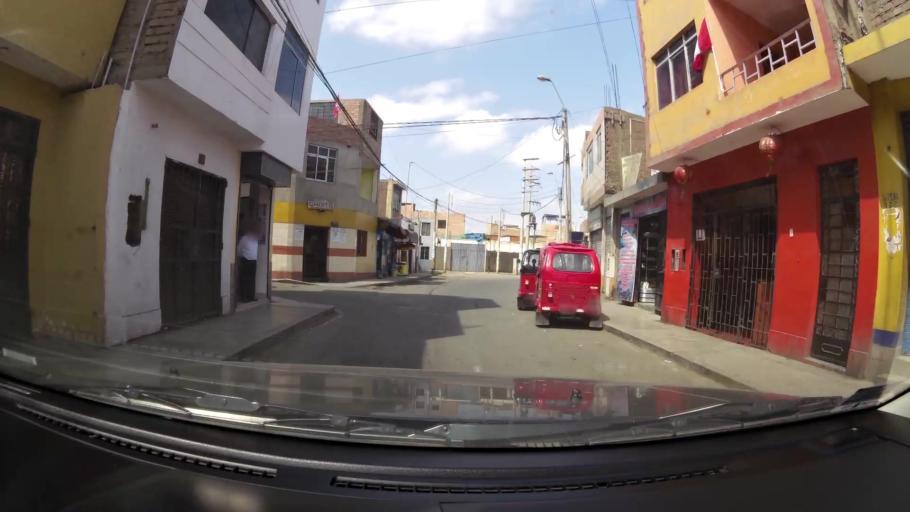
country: PE
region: Lima
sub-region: Provincia de Canete
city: Mala
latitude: -12.6583
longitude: -76.6326
